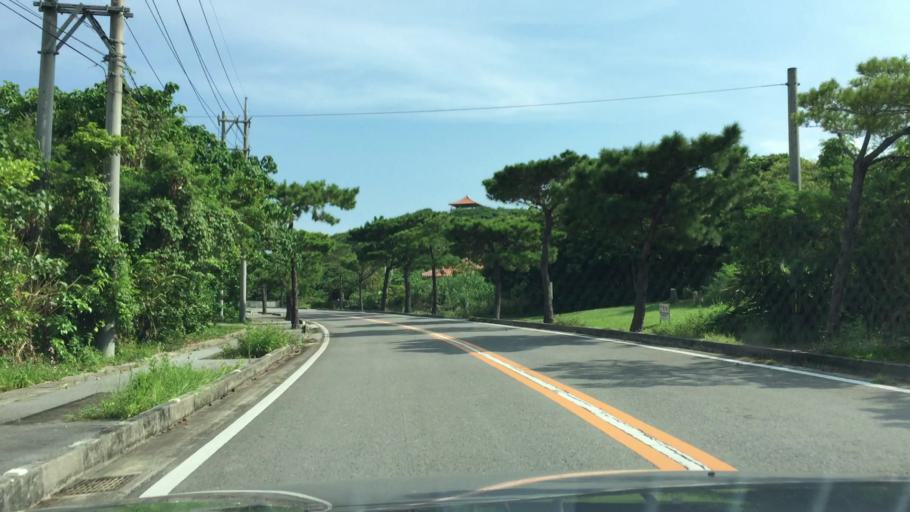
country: JP
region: Okinawa
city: Ishigaki
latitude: 24.4931
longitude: 124.2794
